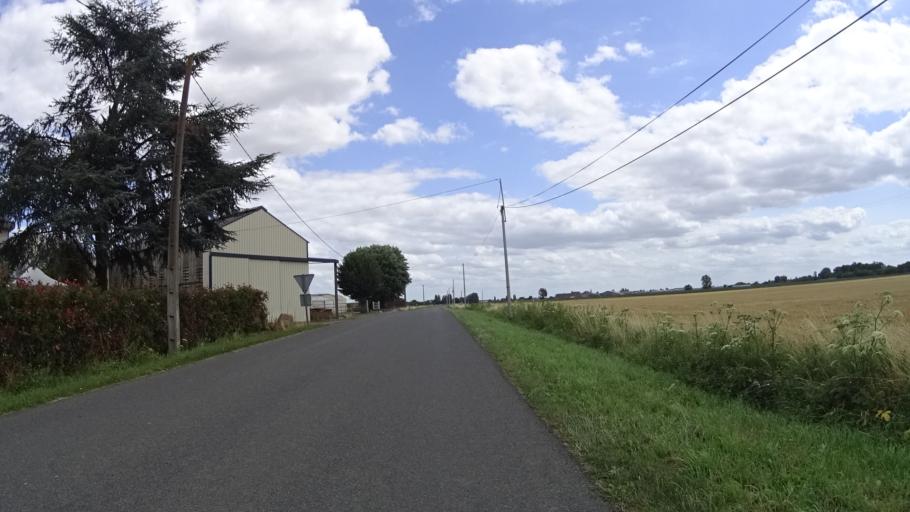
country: FR
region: Pays de la Loire
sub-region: Departement de Maine-et-Loire
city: Saint-Mathurin-sur-Loire
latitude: 47.4105
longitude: -0.2938
